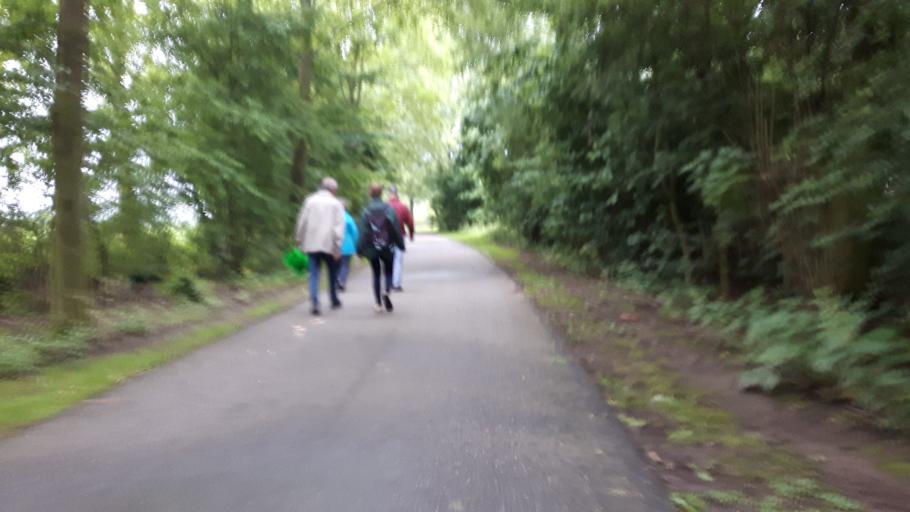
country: NL
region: Utrecht
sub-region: Gemeente Lopik
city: Lopik
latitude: 51.9701
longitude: 4.9594
